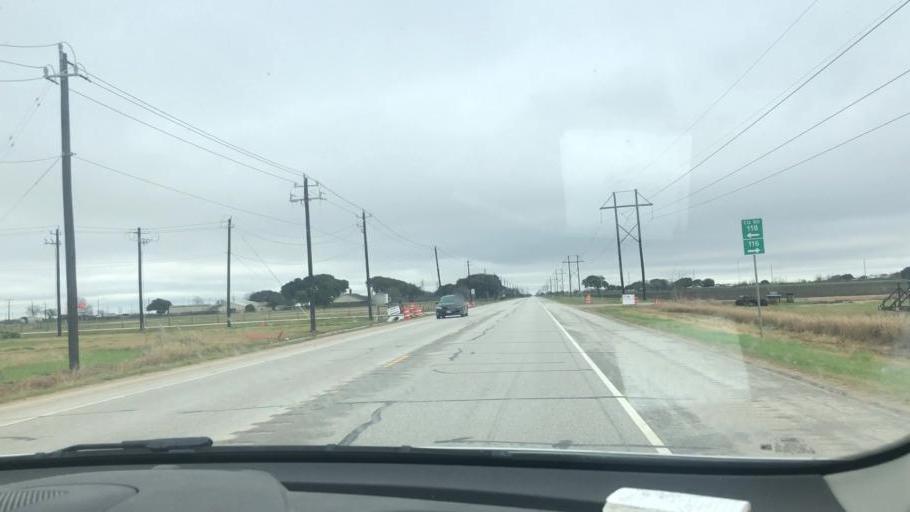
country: US
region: Texas
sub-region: Wharton County
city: Boling
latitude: 29.2059
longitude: -96.0236
